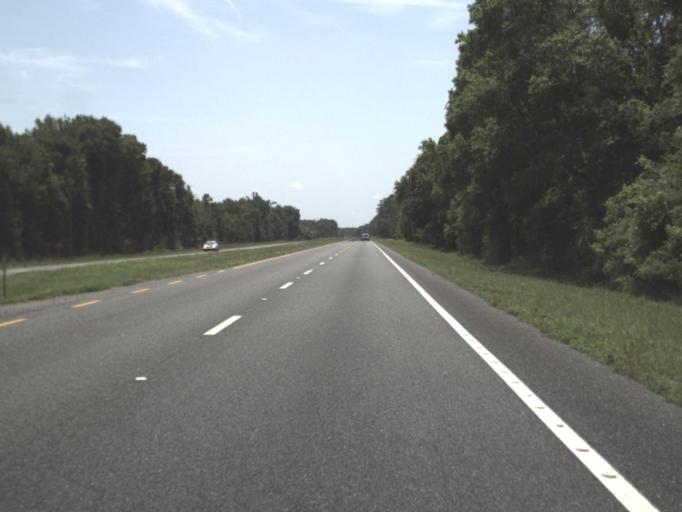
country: US
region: Florida
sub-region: Taylor County
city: Steinhatchee
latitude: 29.8934
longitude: -83.4178
